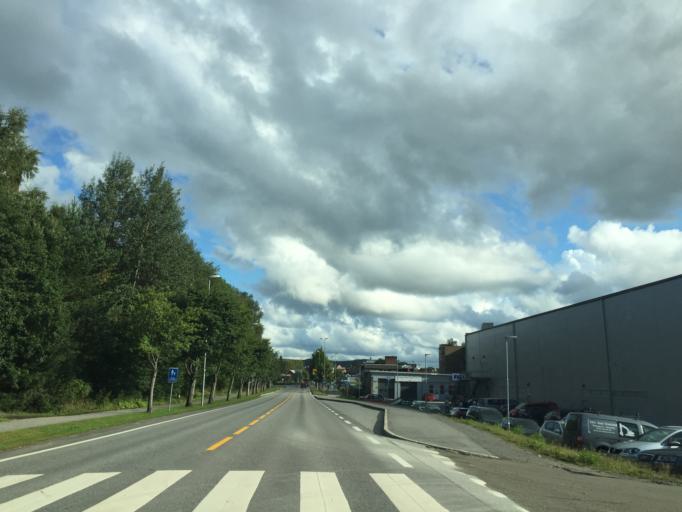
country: NO
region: Hedmark
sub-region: Kongsvinger
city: Kongsvinger
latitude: 60.1952
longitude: 11.9894
